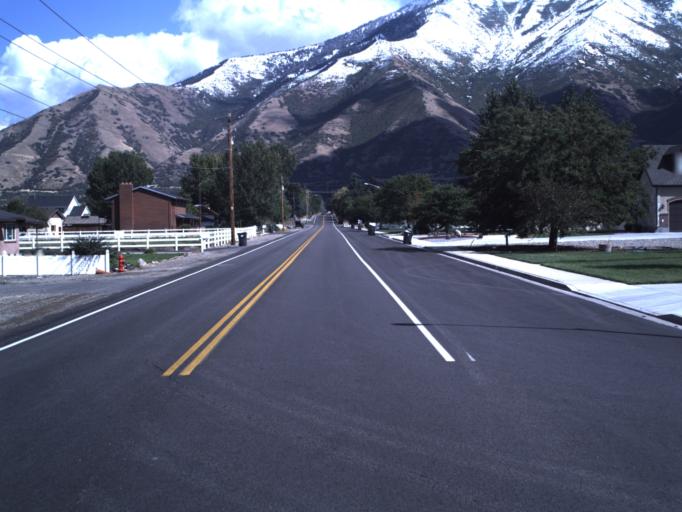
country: US
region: Utah
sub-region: Utah County
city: Mapleton
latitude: 40.1157
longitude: -111.5881
